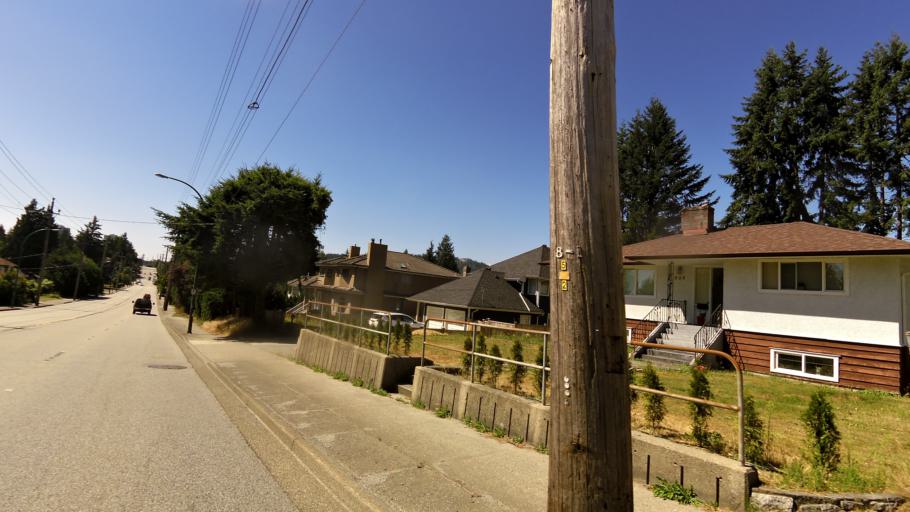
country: CA
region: British Columbia
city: Port Moody
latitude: 49.2636
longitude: -122.8707
